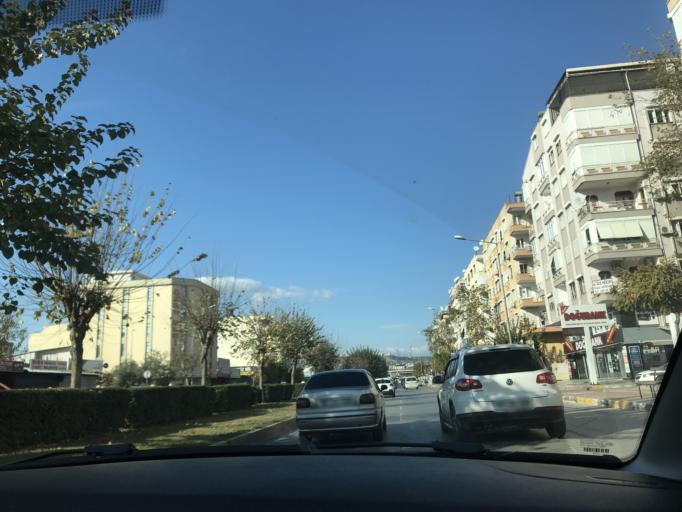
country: TR
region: Antalya
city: Antalya
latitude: 36.9079
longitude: 30.6993
